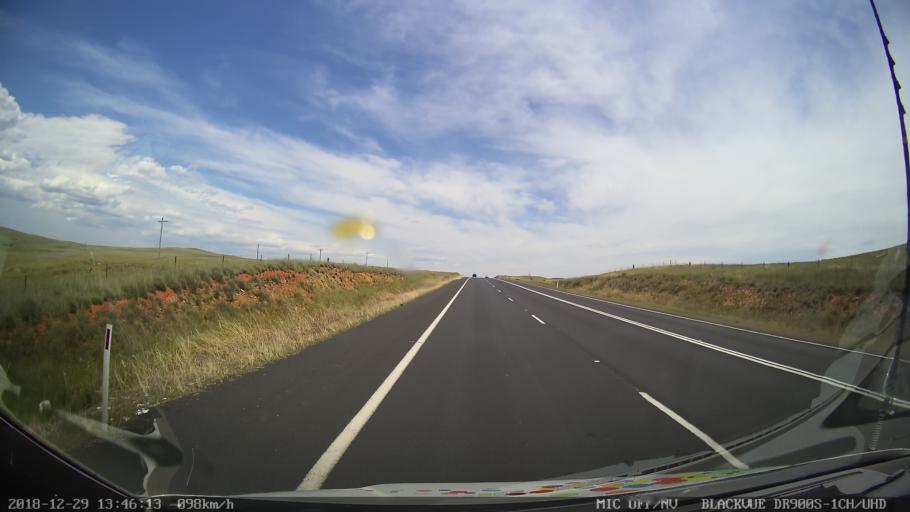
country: AU
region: New South Wales
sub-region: Cooma-Monaro
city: Cooma
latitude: -36.1084
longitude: 149.1433
